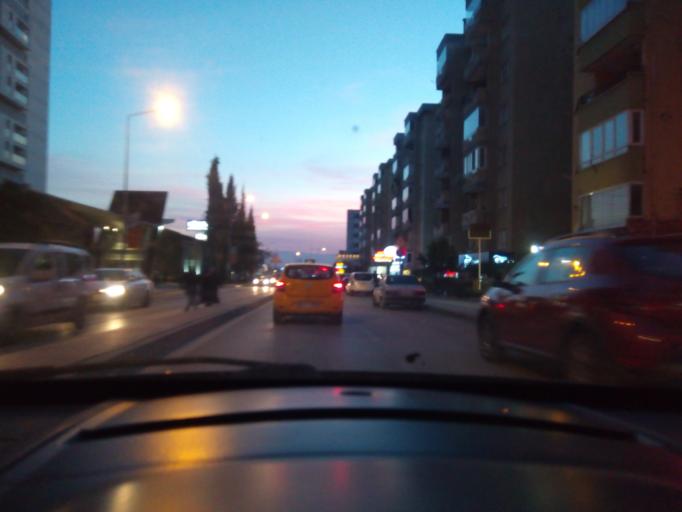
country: TR
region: Bursa
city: Niluefer
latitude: 40.2535
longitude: 28.9579
